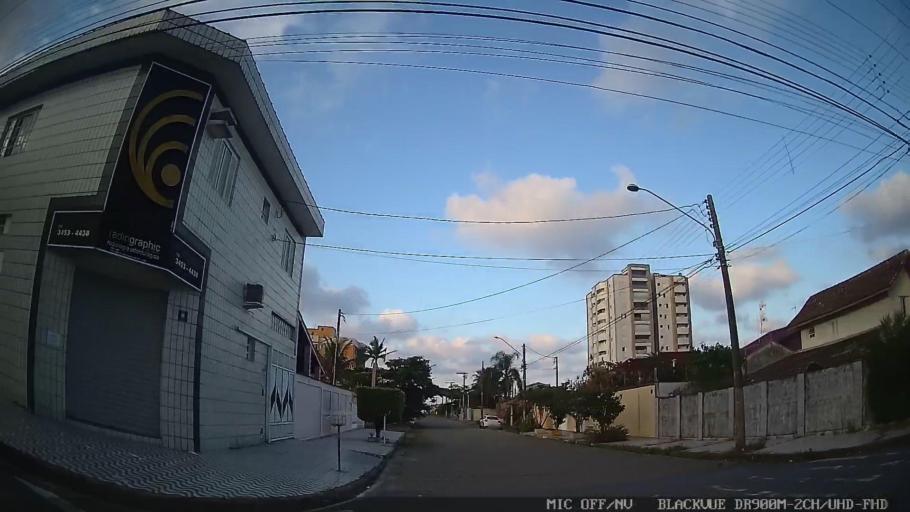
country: BR
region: Sao Paulo
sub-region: Peruibe
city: Peruibe
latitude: -24.3183
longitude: -46.9977
